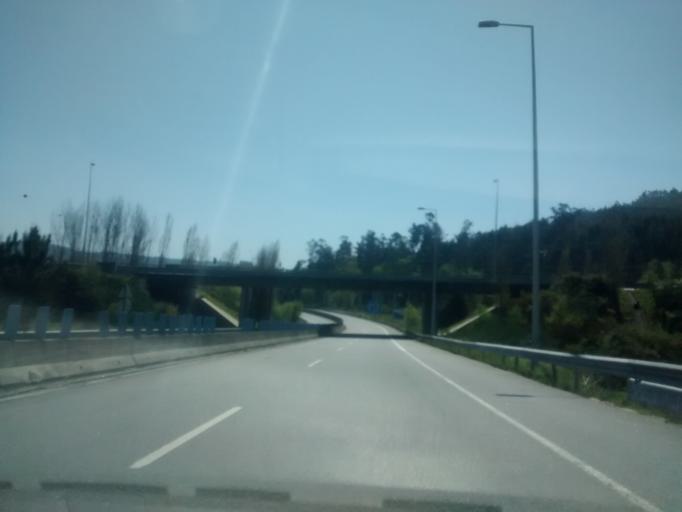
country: PT
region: Braga
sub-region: Braga
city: Oliveira
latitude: 41.5082
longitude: -8.4467
